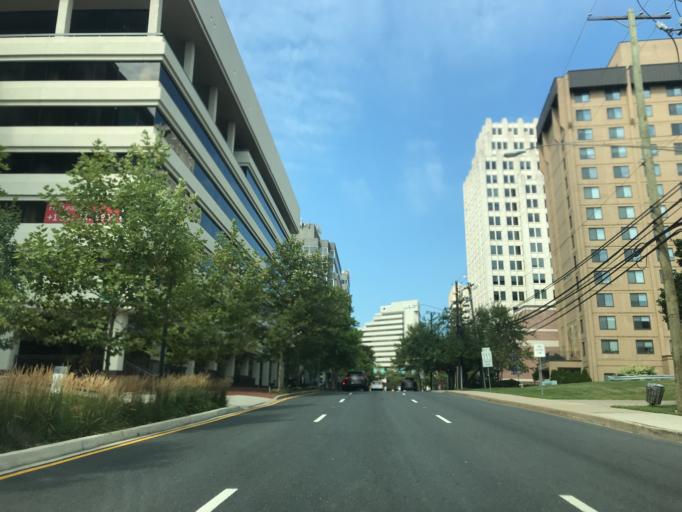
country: US
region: Maryland
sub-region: Montgomery County
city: Bethesda
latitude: 38.9850
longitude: -77.0912
